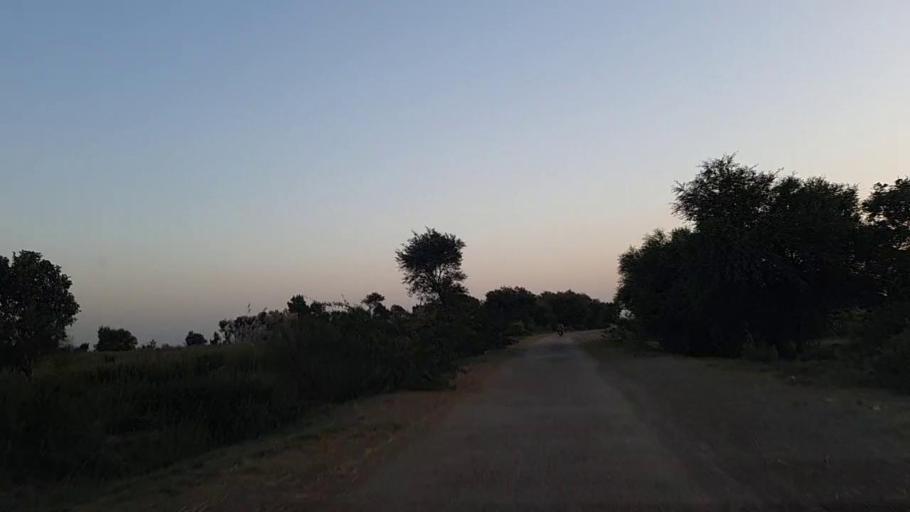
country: PK
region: Sindh
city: Mirpur Batoro
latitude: 24.6184
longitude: 68.1838
